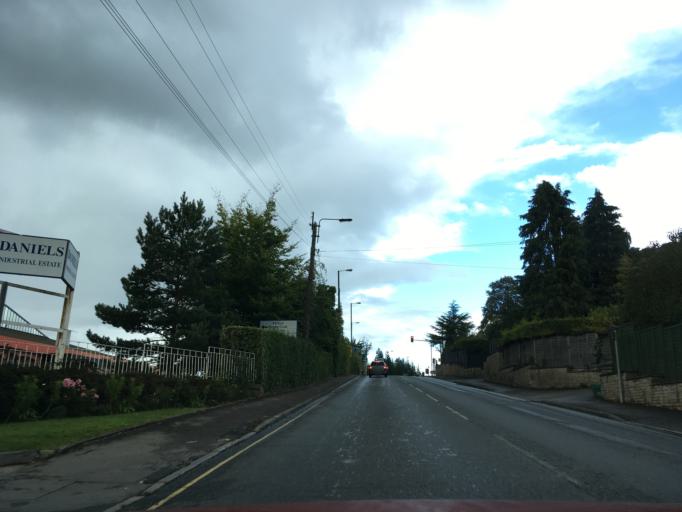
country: GB
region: England
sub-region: Gloucestershire
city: Stroud
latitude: 51.7374
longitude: -2.2322
